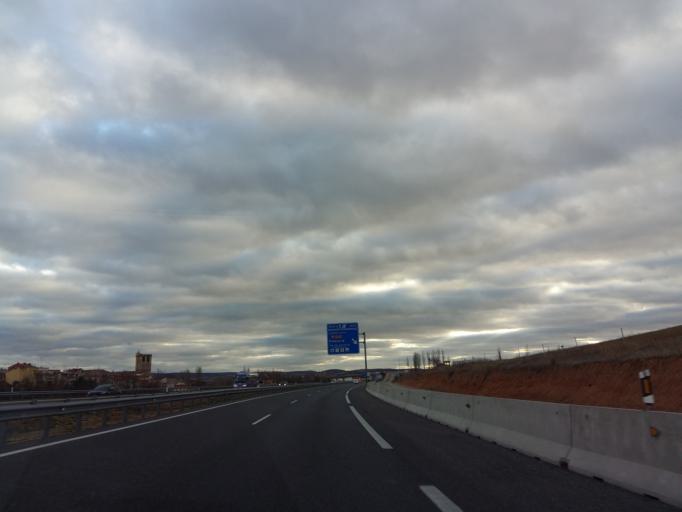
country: ES
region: Castille and Leon
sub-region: Provincia de Burgos
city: Villalmanzo
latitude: 42.0525
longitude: -3.7438
